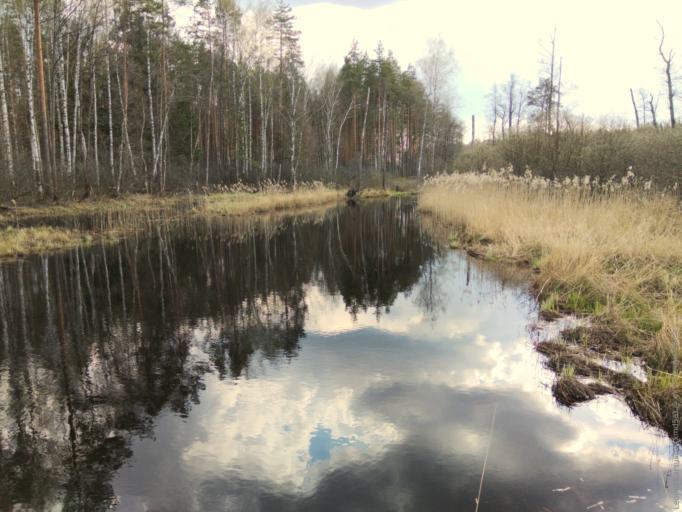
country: RU
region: Vladimir
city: Urshel'skiy
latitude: 55.6752
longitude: 40.2847
